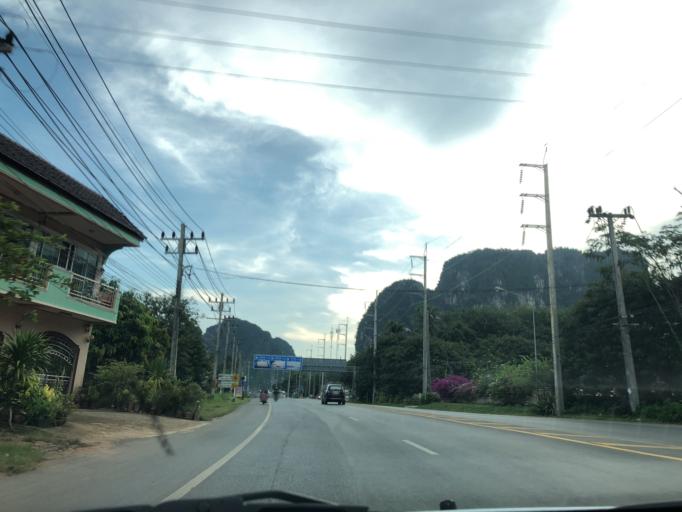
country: TH
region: Krabi
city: Krabi
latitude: 8.0823
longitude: 98.8611
